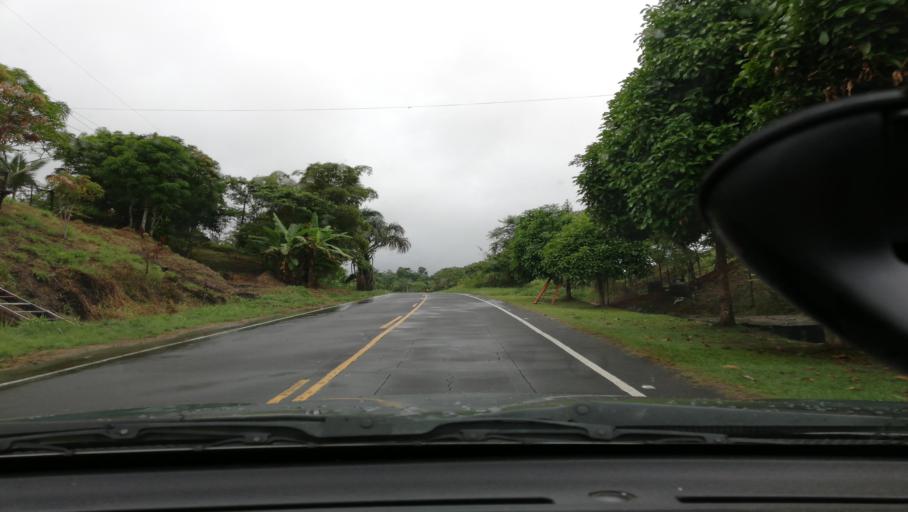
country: PE
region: Loreto
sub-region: Provincia de Loreto
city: Nauta
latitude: -4.2165
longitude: -73.4833
